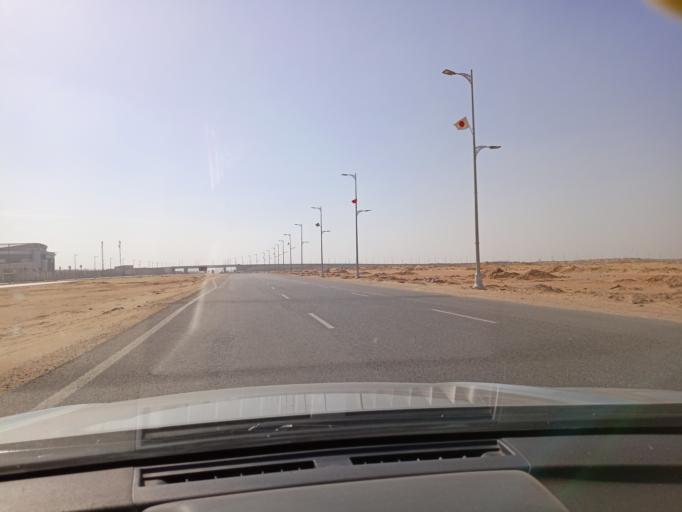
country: EG
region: Muhafazat al Qalyubiyah
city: Al Khankah
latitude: 30.0444
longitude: 31.6935
